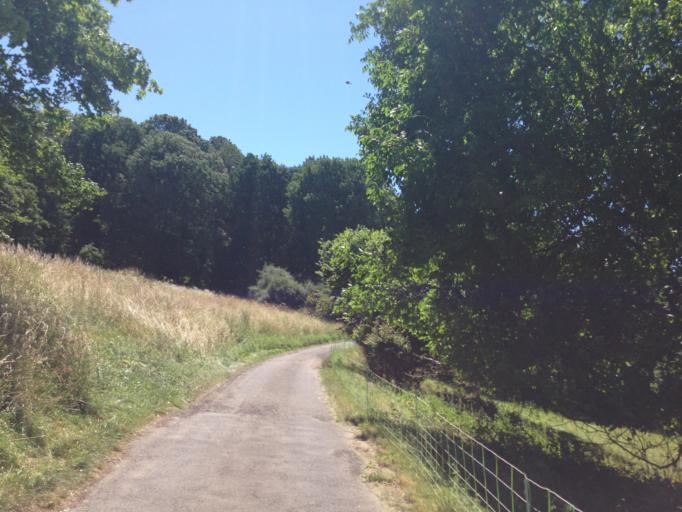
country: DE
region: Hesse
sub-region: Regierungsbezirk Giessen
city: Reiskirchen
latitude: 50.5944
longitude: 8.8230
